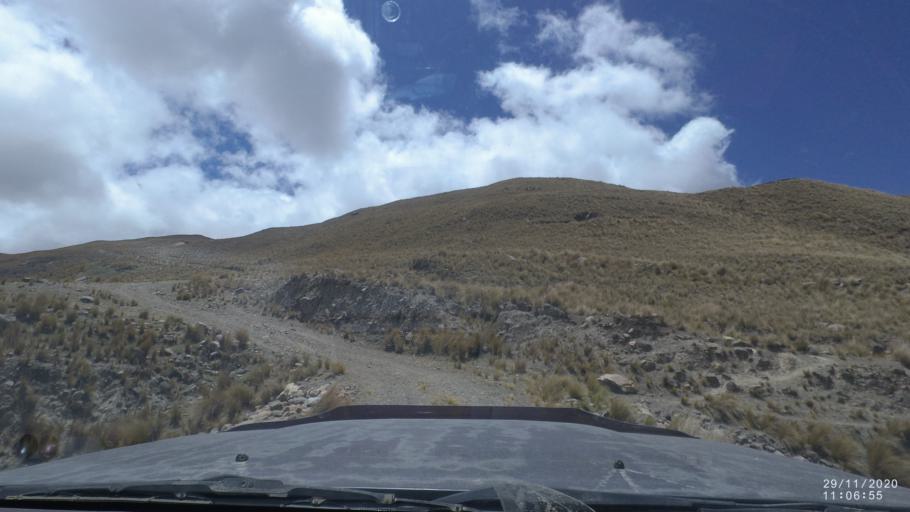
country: BO
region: Cochabamba
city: Cochabamba
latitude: -17.1865
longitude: -66.2085
